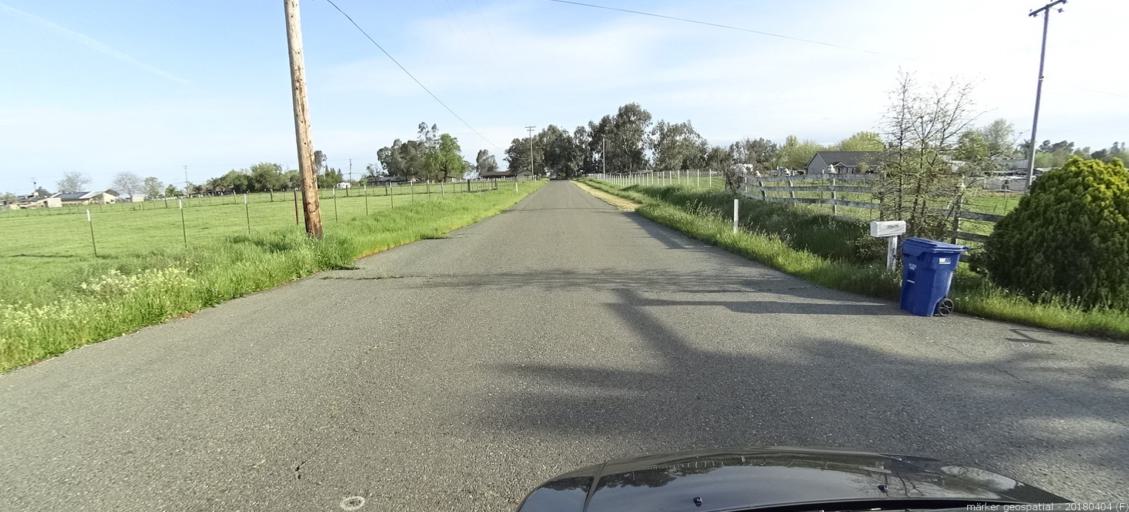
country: US
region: California
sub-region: Sacramento County
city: Herald
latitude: 38.3414
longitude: -121.2467
